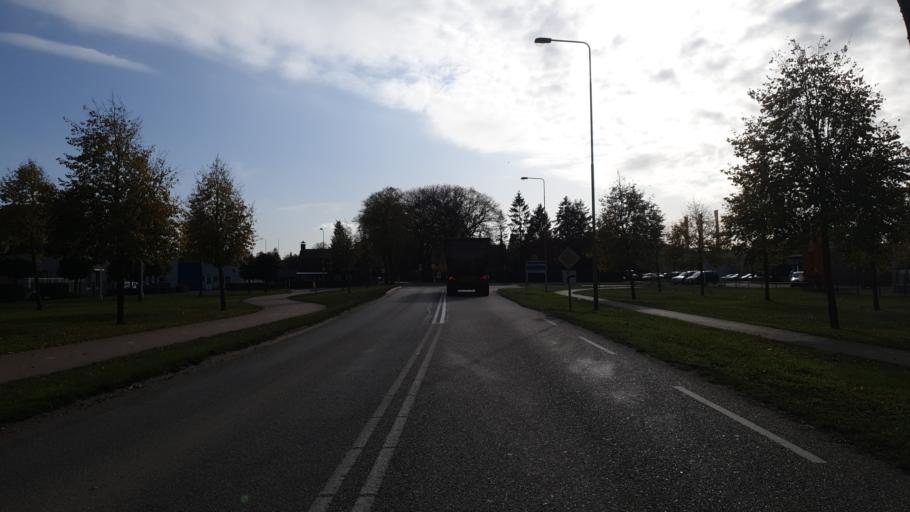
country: NL
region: Limburg
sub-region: Gemeente Gennep
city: Gennep
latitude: 51.6784
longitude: 5.9753
